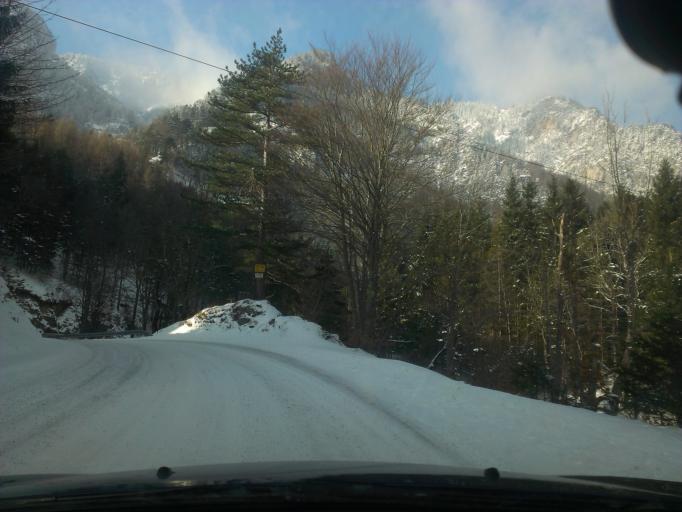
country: AT
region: Lower Austria
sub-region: Politischer Bezirk Neunkirchen
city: Reichenau an der Rax
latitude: 47.7367
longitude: 15.7890
